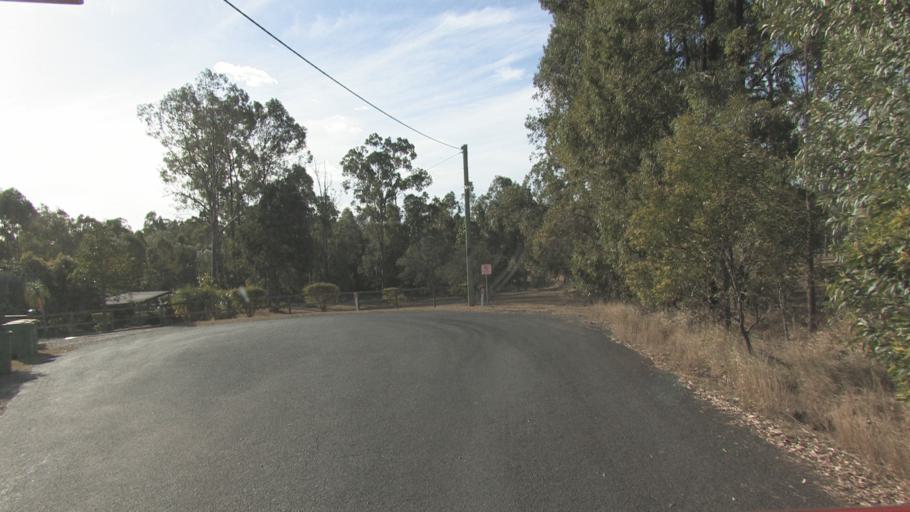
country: AU
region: Queensland
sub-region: Logan
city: Cedar Vale
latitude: -27.8711
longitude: 153.0087
